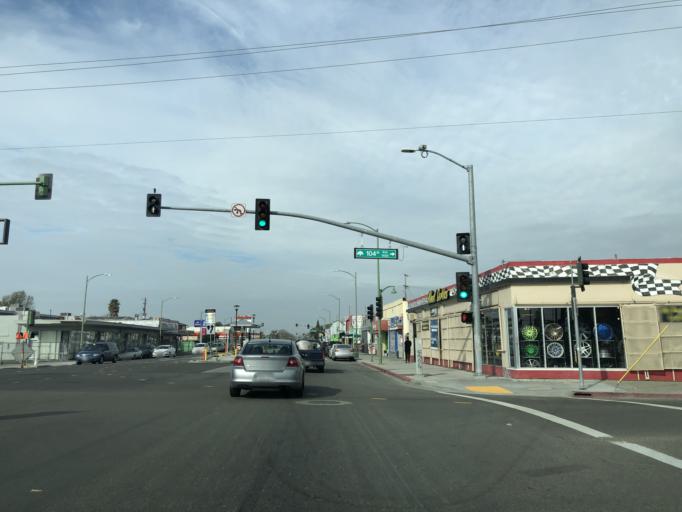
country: US
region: California
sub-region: Alameda County
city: San Leandro
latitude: 37.7402
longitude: -122.1673
